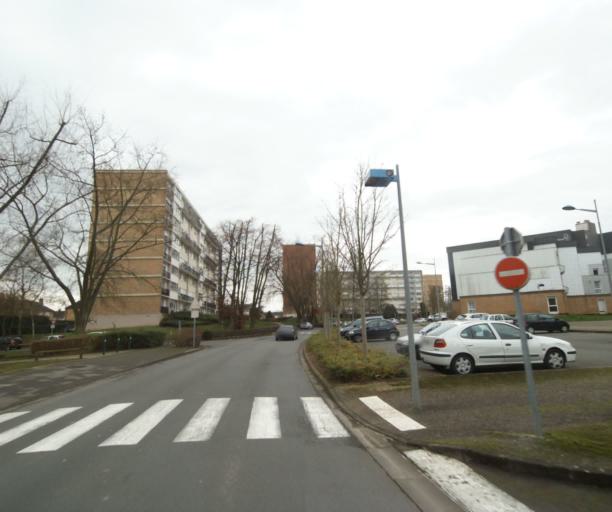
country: FR
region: Nord-Pas-de-Calais
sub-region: Departement du Nord
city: Saint-Saulve
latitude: 50.3671
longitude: 3.5612
